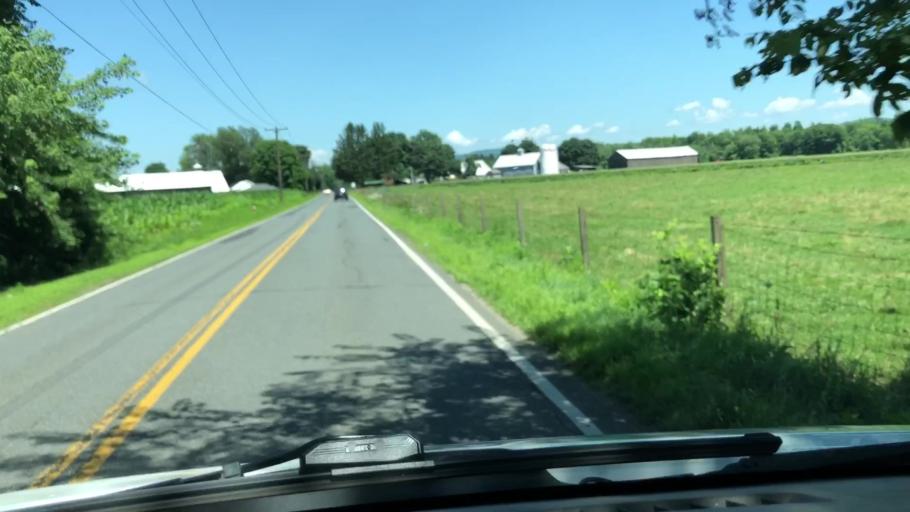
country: US
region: Massachusetts
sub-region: Hampshire County
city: North Amherst
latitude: 42.4018
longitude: -72.5447
